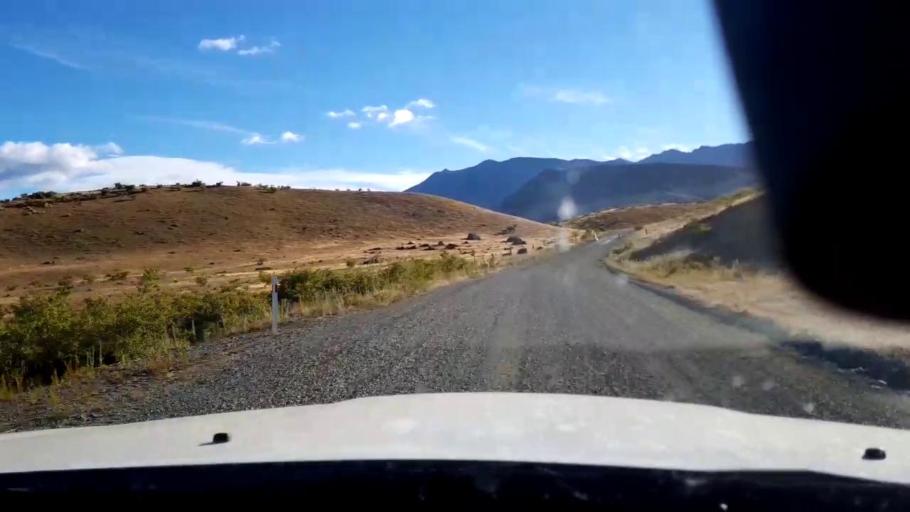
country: NZ
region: Canterbury
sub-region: Timaru District
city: Pleasant Point
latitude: -43.9661
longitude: 170.5192
